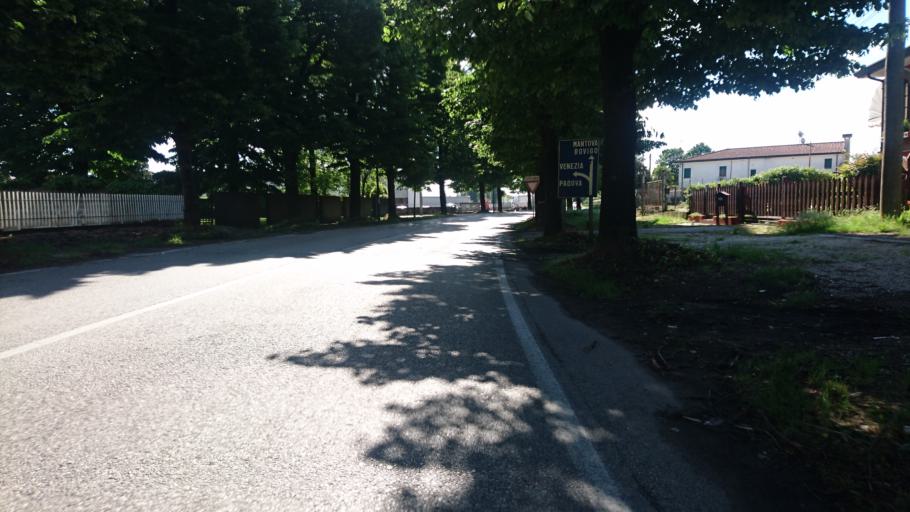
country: IT
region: Veneto
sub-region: Provincia di Padova
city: Monselice
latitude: 45.2444
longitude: 11.7573
